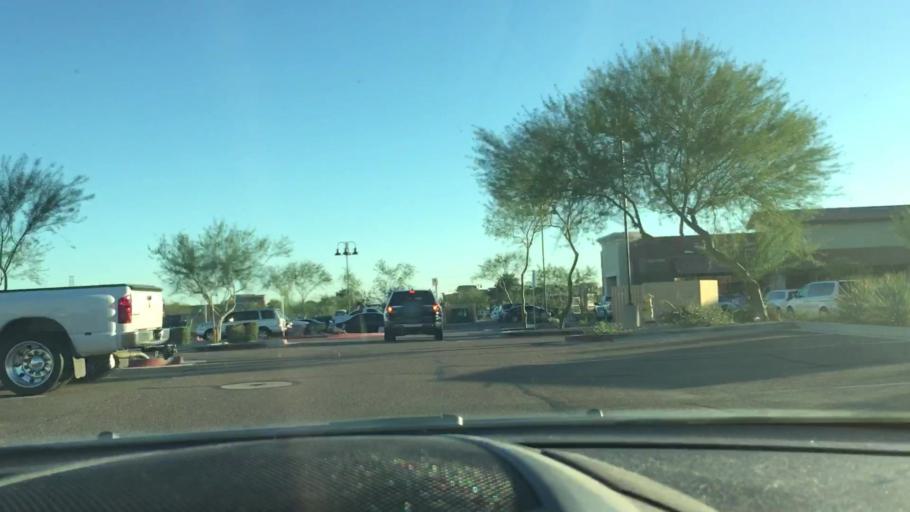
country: US
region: Arizona
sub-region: Maricopa County
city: Sun City West
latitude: 33.7121
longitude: -112.2707
